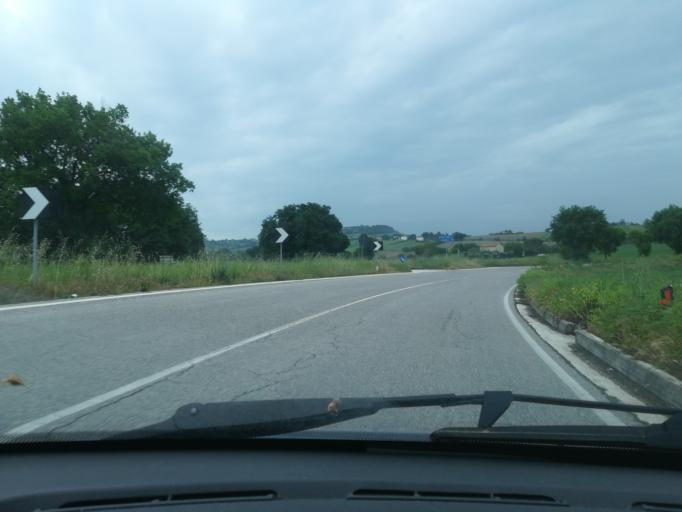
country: IT
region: The Marches
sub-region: Provincia di Macerata
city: Pollenza
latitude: 43.2938
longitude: 13.3780
